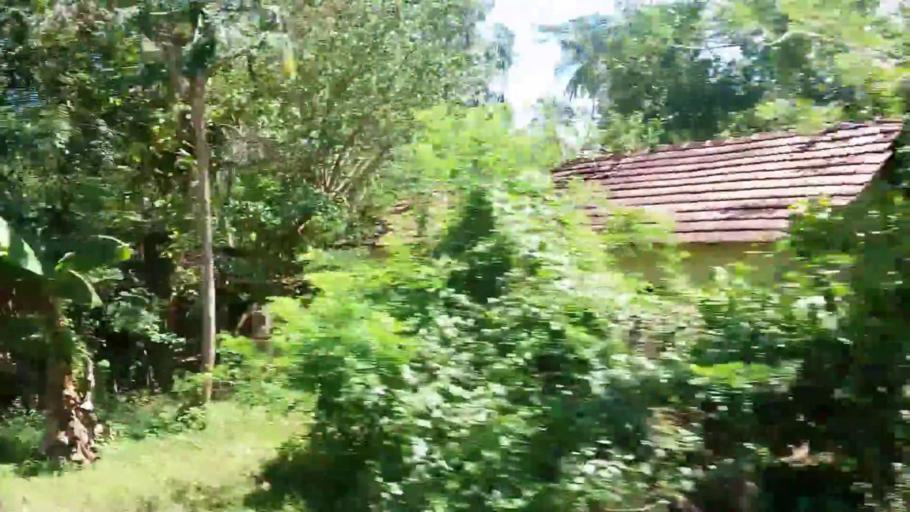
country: LK
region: Southern
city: Hikkaduwa
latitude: 6.1791
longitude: 80.0784
